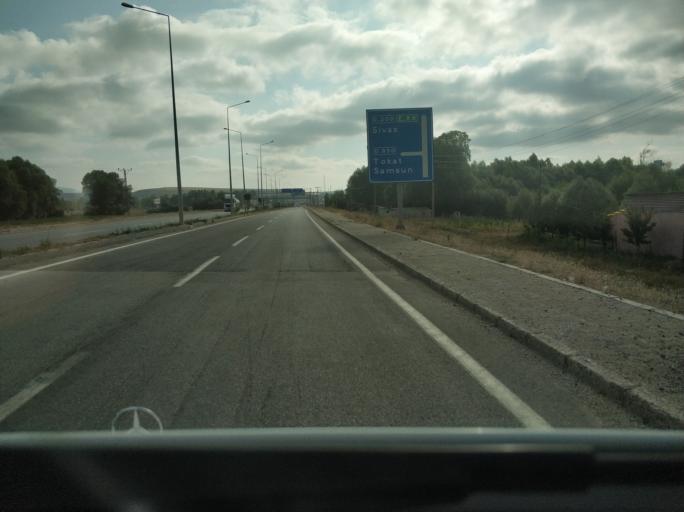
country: TR
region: Sivas
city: Yildizeli
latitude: 39.8689
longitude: 36.5852
